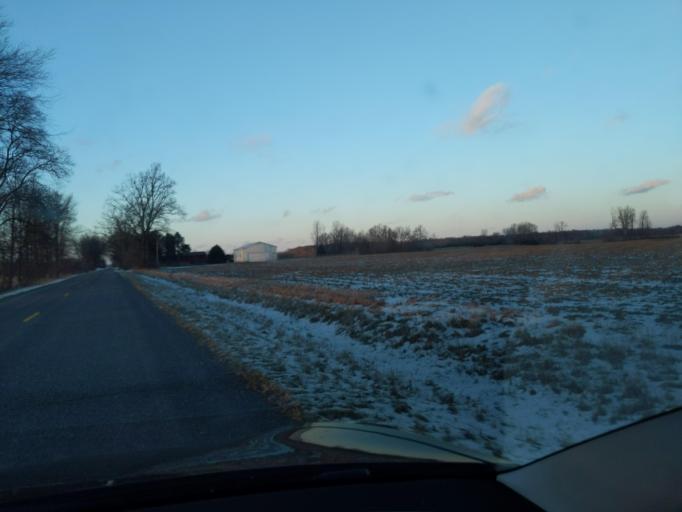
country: US
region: Michigan
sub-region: Ingham County
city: Stockbridge
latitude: 42.4580
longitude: -84.2779
